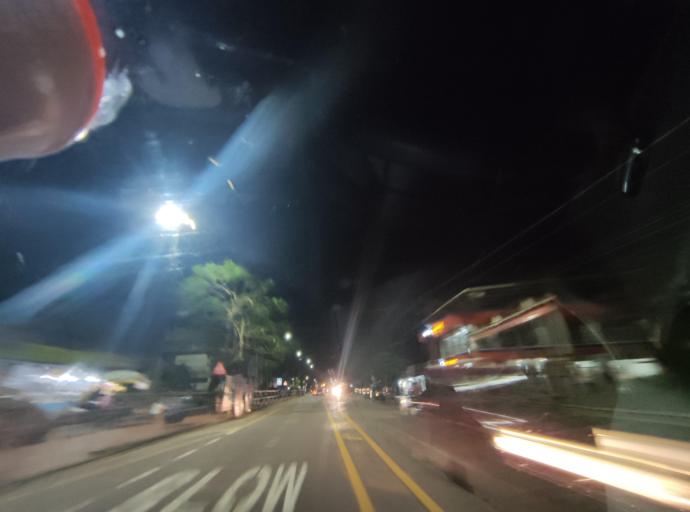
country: IN
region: Kerala
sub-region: Thiruvananthapuram
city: Attingal
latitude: 8.7548
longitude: 76.8942
